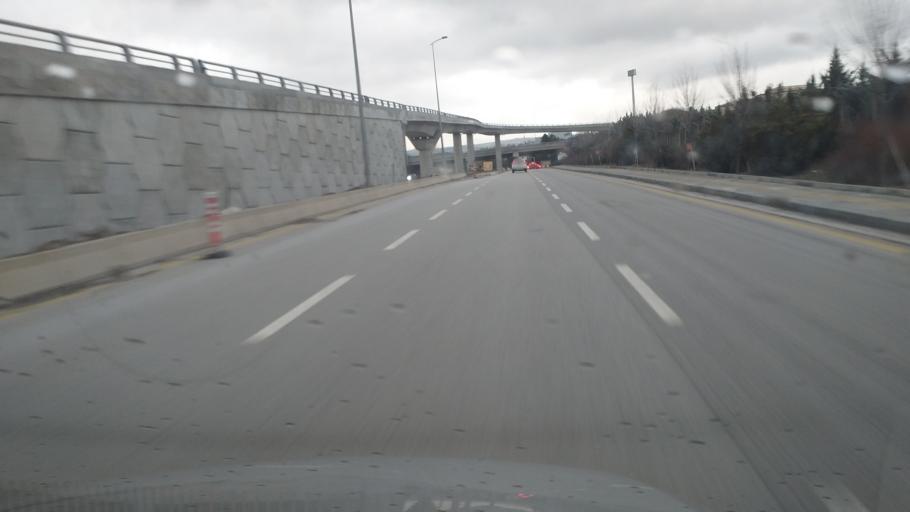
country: TR
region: Ankara
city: Batikent
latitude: 39.8992
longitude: 32.7333
